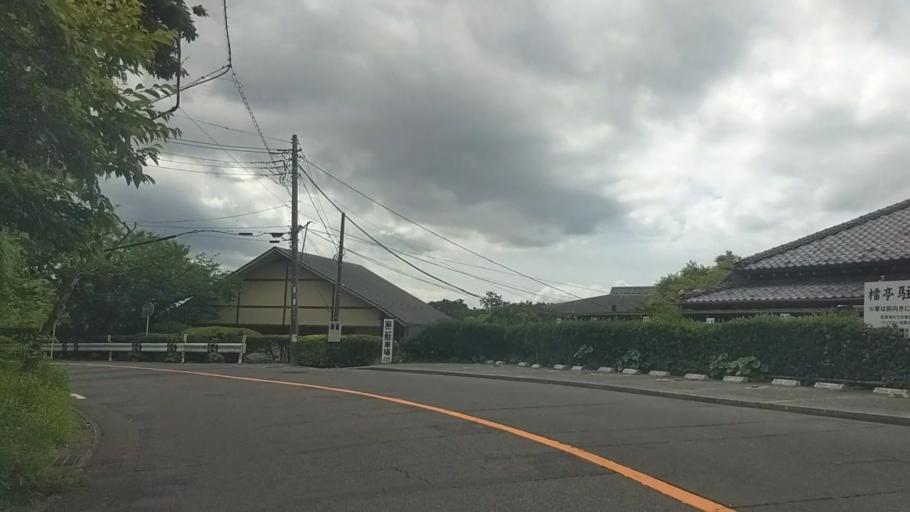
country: JP
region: Kanagawa
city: Kamakura
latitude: 35.3168
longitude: 139.5151
